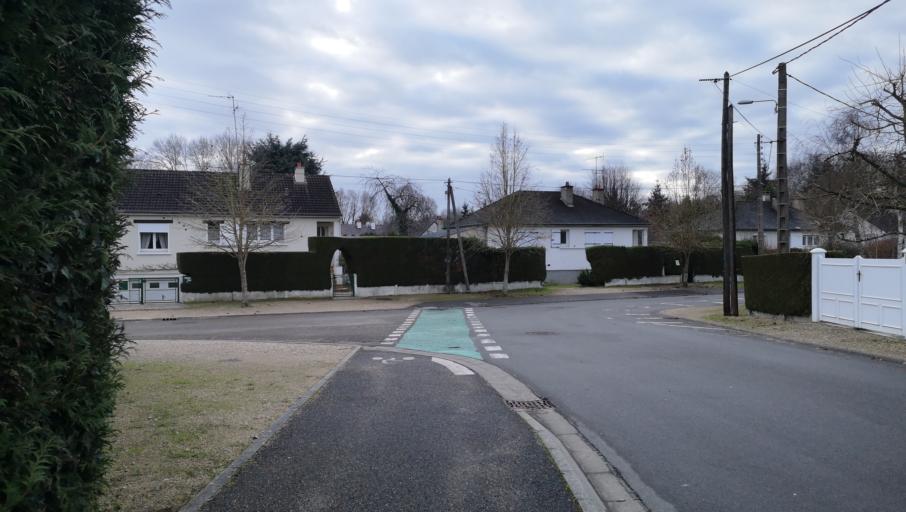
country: FR
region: Centre
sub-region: Departement du Loiret
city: Boigny-sur-Bionne
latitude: 47.9201
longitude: 2.0061
